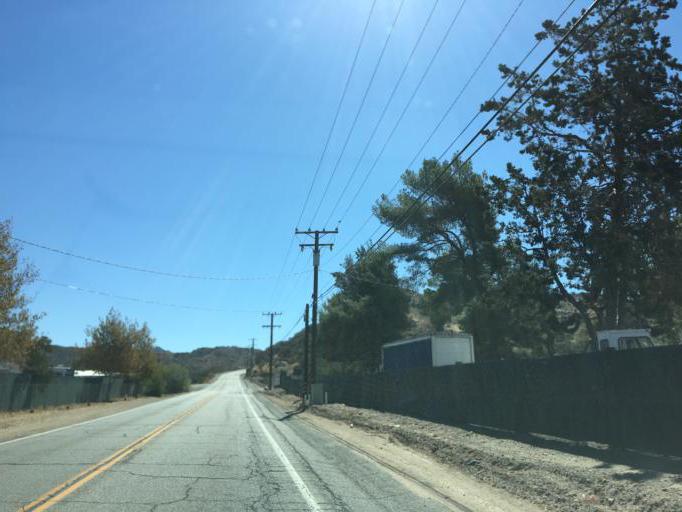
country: US
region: California
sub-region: Los Angeles County
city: Agua Dulce
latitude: 34.4819
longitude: -118.3870
